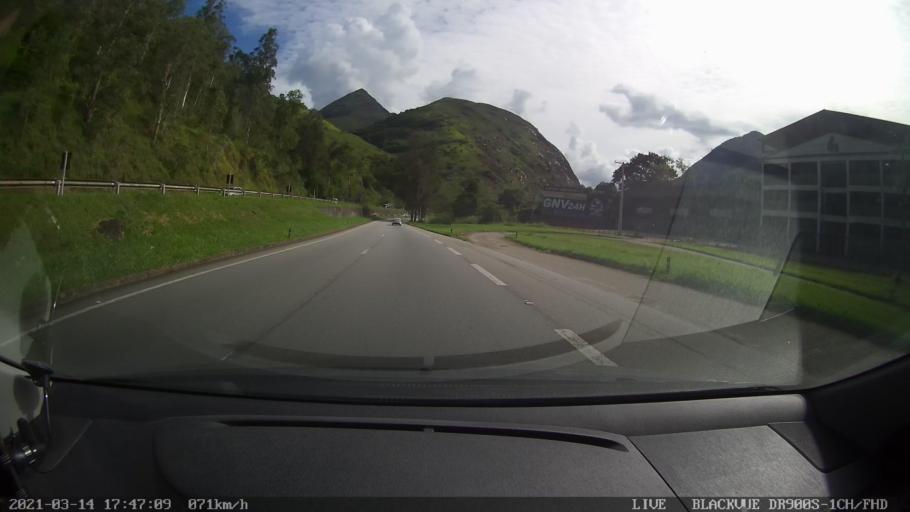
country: BR
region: Rio de Janeiro
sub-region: Petropolis
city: Petropolis
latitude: -22.4351
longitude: -43.1742
